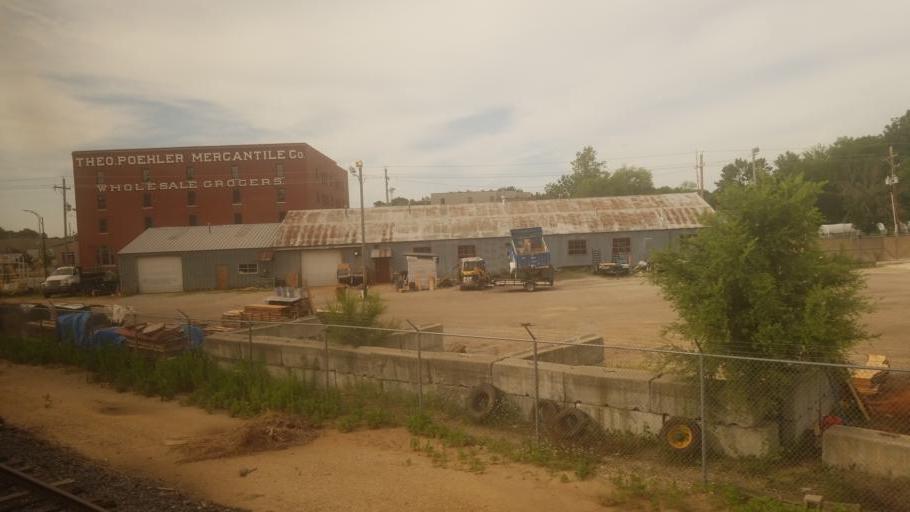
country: US
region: Kansas
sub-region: Douglas County
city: Lawrence
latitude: 38.9701
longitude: -95.2286
